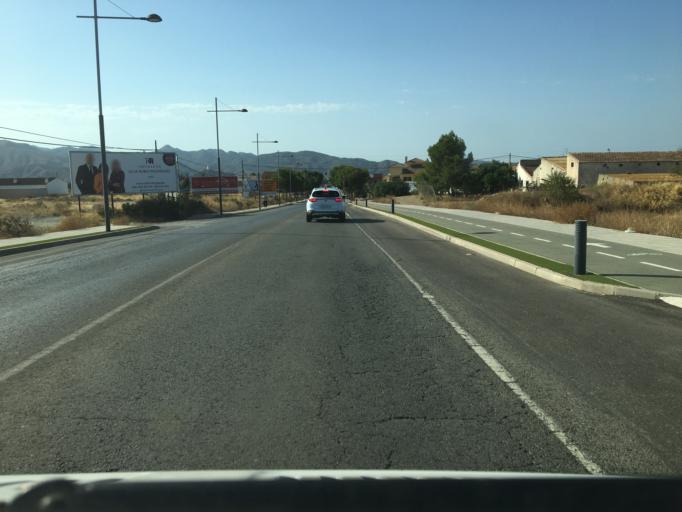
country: ES
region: Andalusia
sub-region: Provincia de Almeria
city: Huercal-Overa
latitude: 37.4051
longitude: -1.9561
